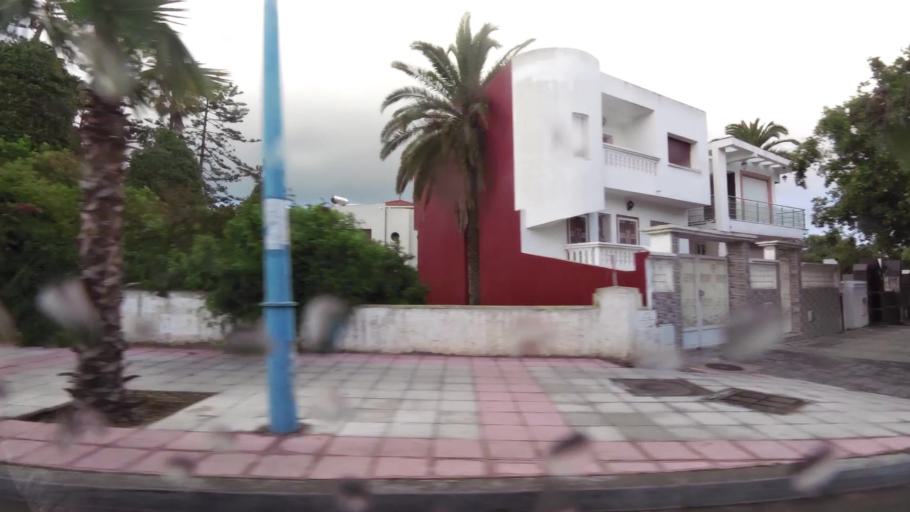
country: MA
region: Doukkala-Abda
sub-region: El-Jadida
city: El Jadida
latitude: 33.2453
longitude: -8.5059
